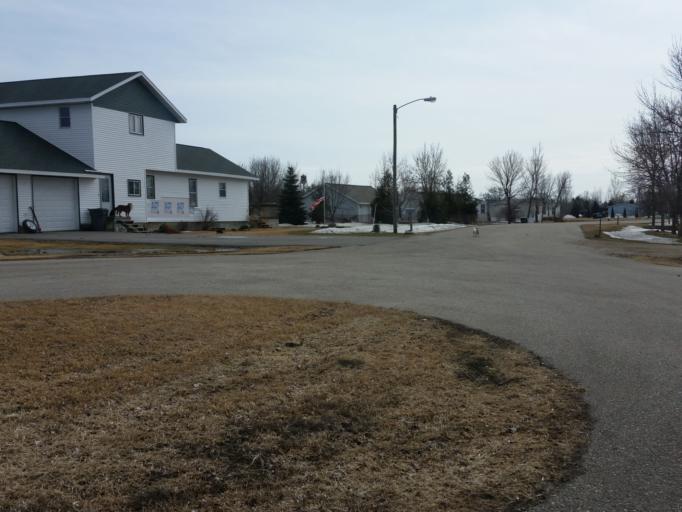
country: US
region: North Dakota
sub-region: Walsh County
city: Grafton
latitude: 48.2950
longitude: -97.3789
